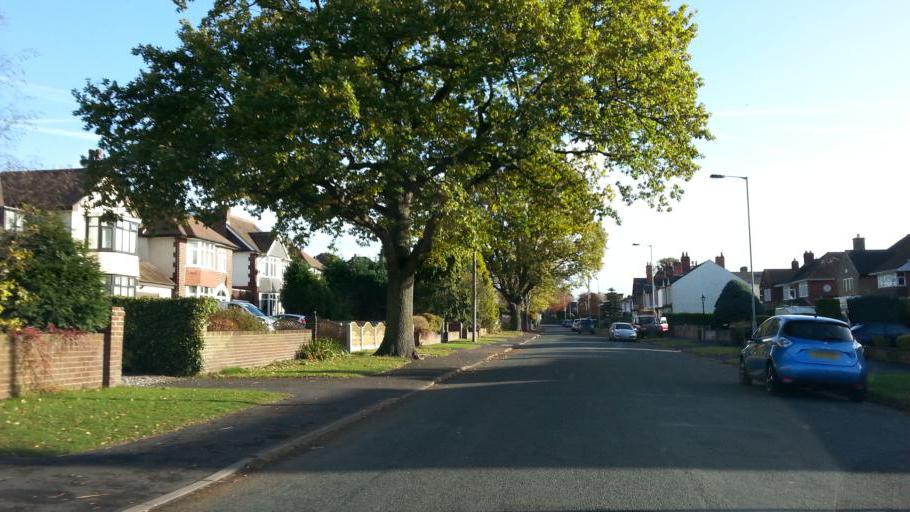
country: GB
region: England
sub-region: Staffordshire
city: Cannock
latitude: 52.6894
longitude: -2.0438
